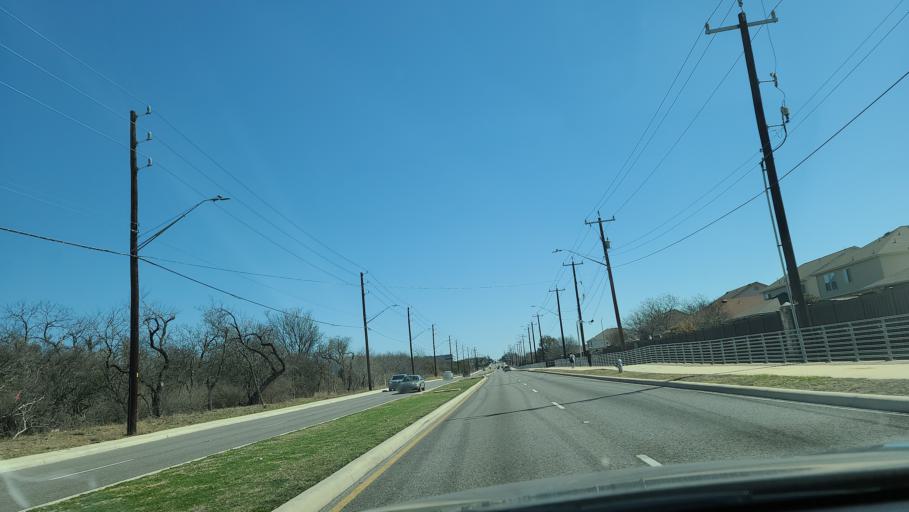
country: US
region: Texas
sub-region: Bexar County
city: Shavano Park
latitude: 29.5724
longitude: -98.6070
